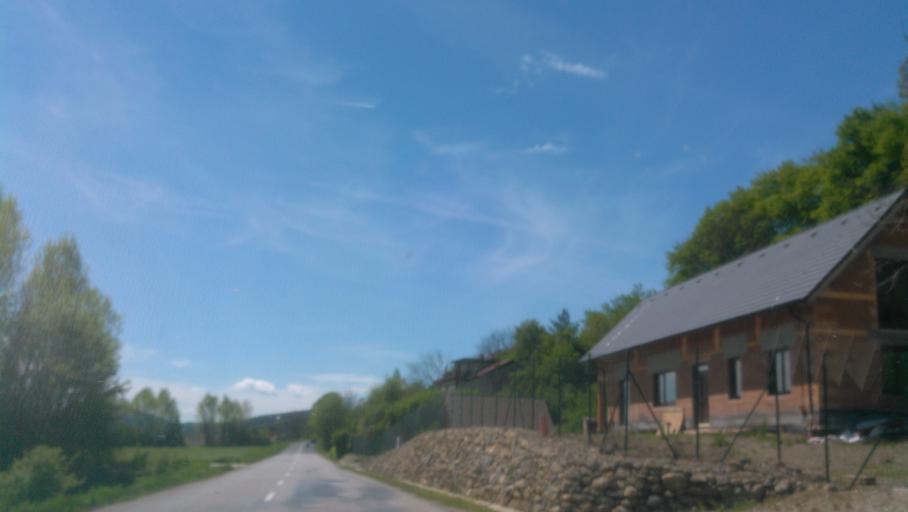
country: SK
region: Banskobystricky
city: Hrochot,Slovakia
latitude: 48.7738
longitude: 19.2915
